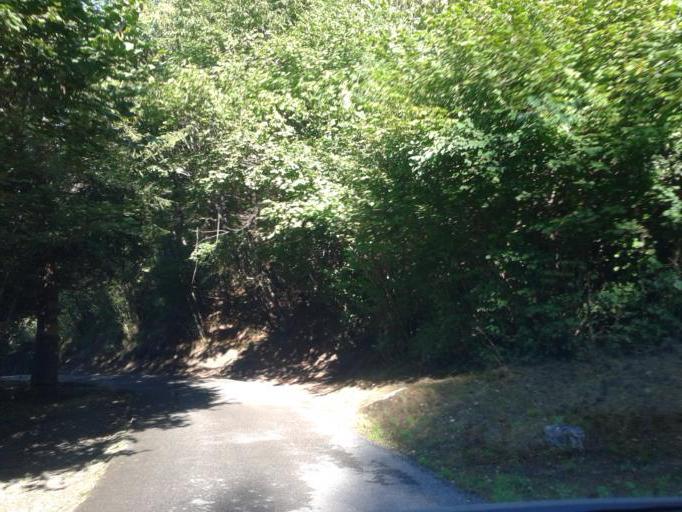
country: IT
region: Trentino-Alto Adige
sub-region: Provincia di Trento
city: Storo
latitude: 45.8500
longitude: 10.5851
